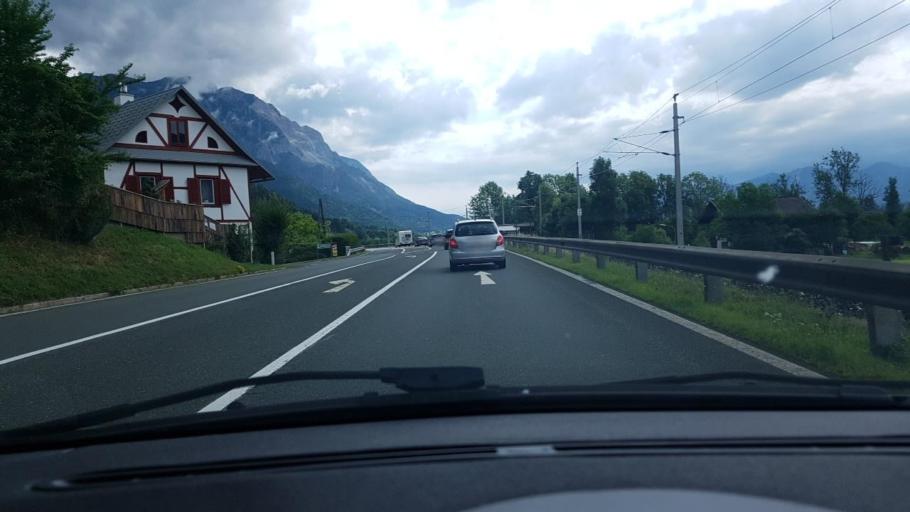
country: AT
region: Carinthia
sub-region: Politischer Bezirk Villach Land
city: Feistritz an der Gail
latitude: 46.5966
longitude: 13.5819
